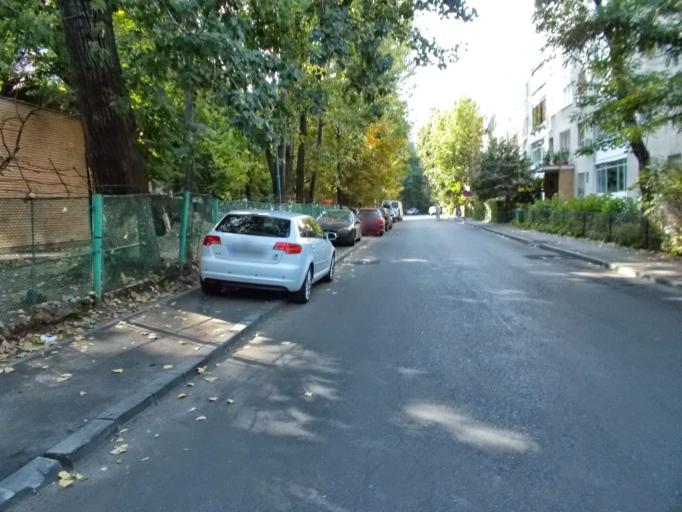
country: RO
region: Bucuresti
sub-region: Municipiul Bucuresti
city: Bucuresti
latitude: 44.3807
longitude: 26.1129
